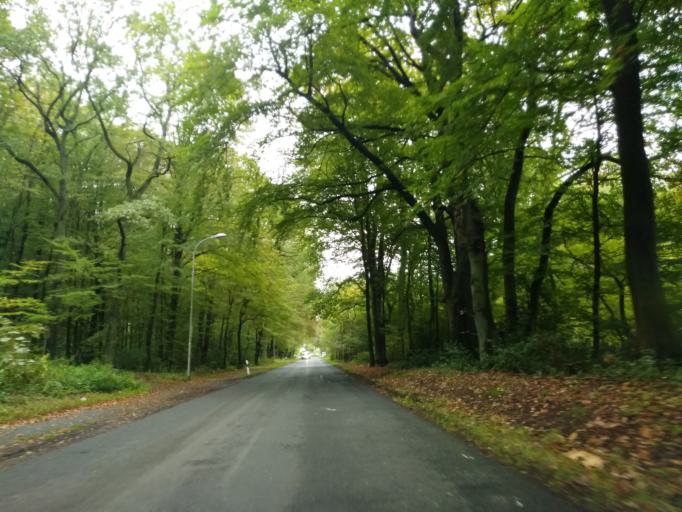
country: DE
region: Rheinland-Pfalz
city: Windhagen
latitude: 50.6422
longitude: 7.3158
